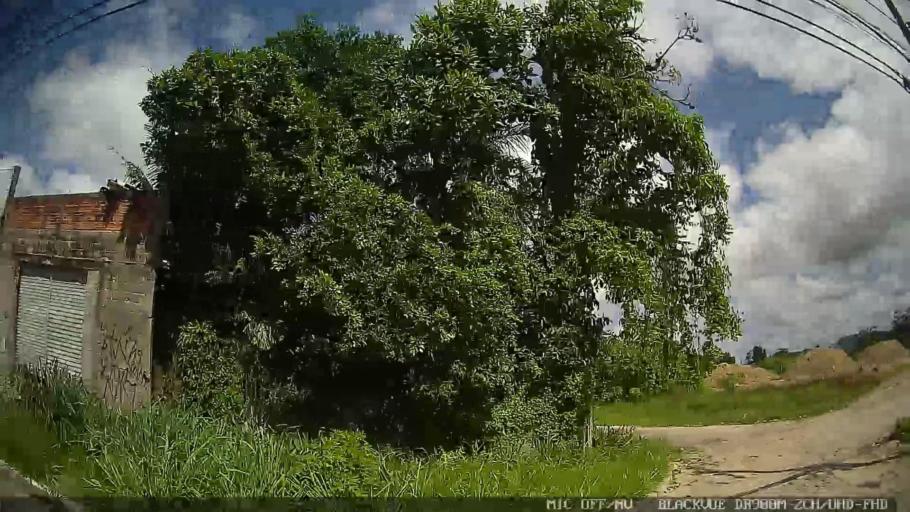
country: BR
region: Sao Paulo
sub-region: Peruibe
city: Peruibe
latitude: -24.3096
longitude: -47.0118
